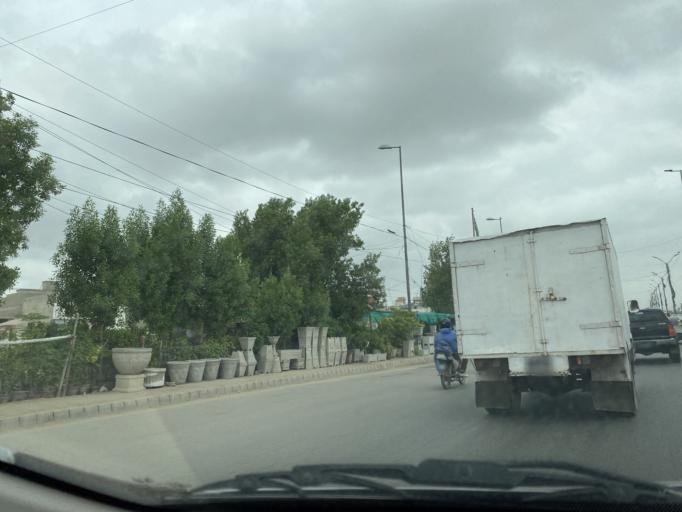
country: PK
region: Sindh
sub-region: Karachi District
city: Karachi
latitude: 24.8635
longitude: 67.0862
